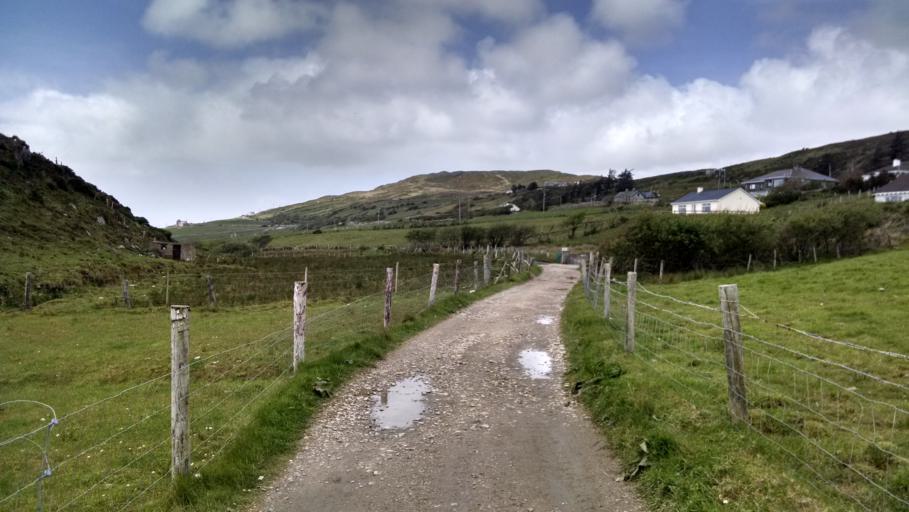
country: IE
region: Connaught
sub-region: County Galway
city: Clifden
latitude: 53.4919
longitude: -10.0511
